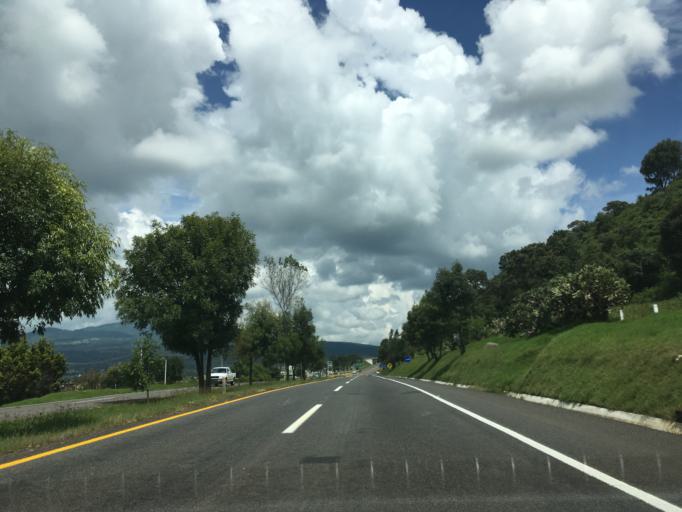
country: MX
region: Michoacan
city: Huiramba
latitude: 19.5544
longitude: -101.4270
